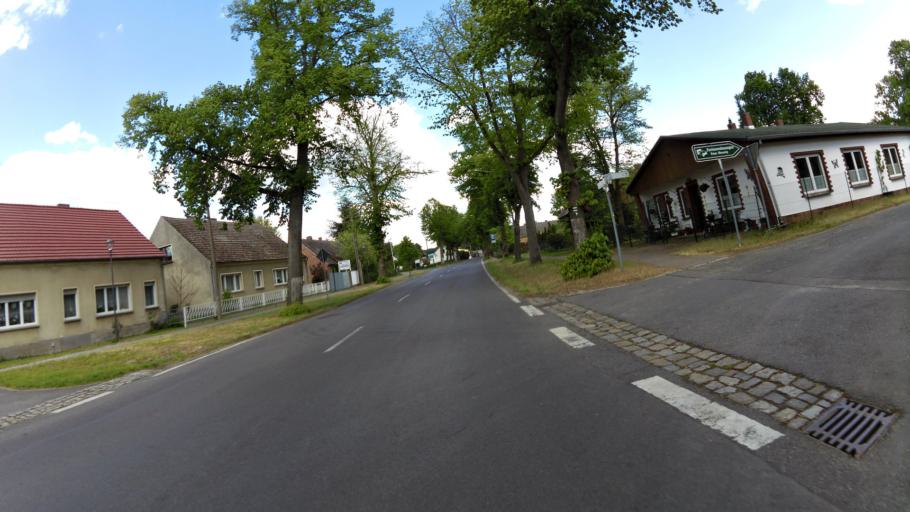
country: DE
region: Brandenburg
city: Schlepzig
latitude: 52.1210
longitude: 13.9494
